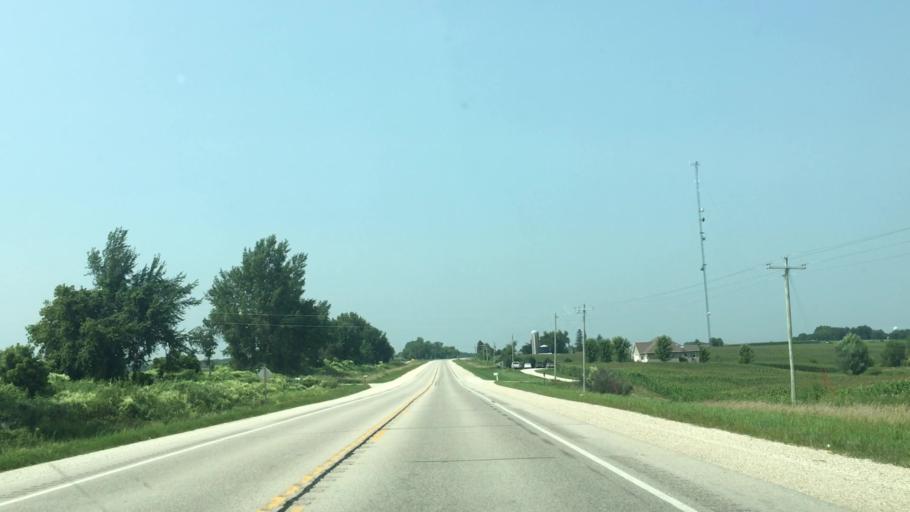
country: US
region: Iowa
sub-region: Winneshiek County
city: Decorah
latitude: 43.1975
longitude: -91.8743
